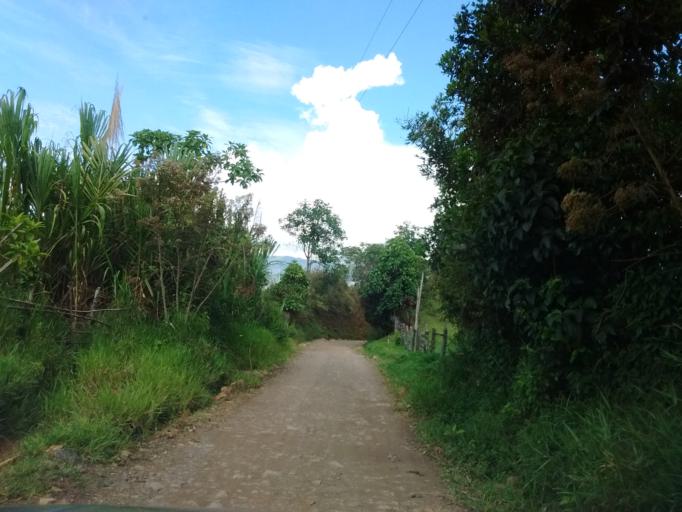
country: CO
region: Cauca
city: Morales
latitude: 2.6876
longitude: -76.7408
